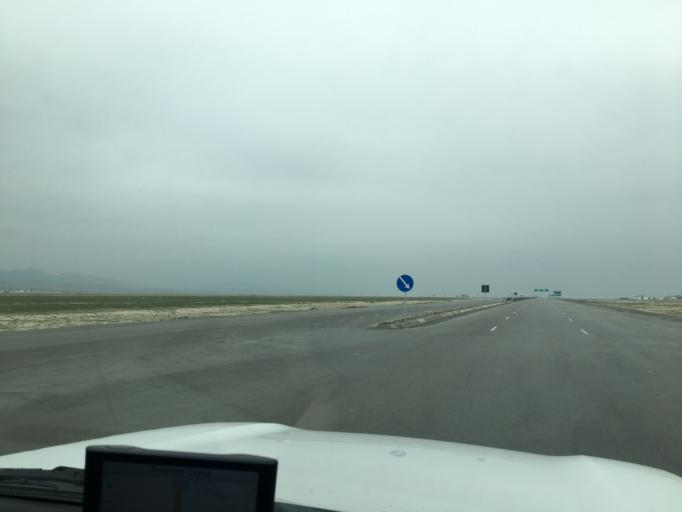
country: IR
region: Razavi Khorasan
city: Dargaz
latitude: 37.7158
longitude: 59.0181
